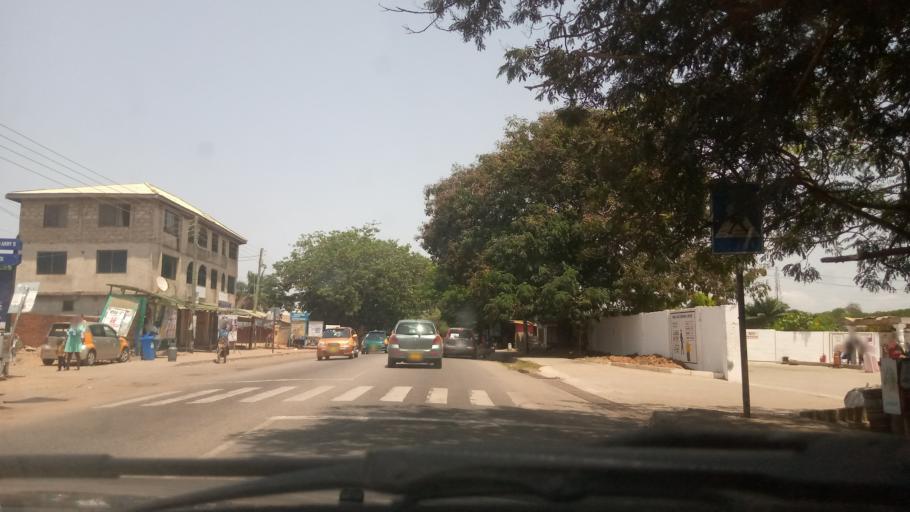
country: GH
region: Greater Accra
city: Accra
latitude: 5.5414
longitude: -0.2394
